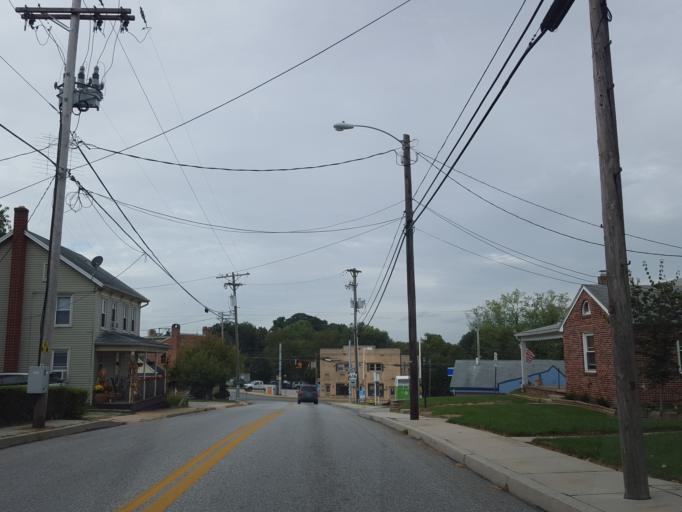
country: US
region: Pennsylvania
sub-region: York County
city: West York
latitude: 39.9020
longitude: -76.7881
